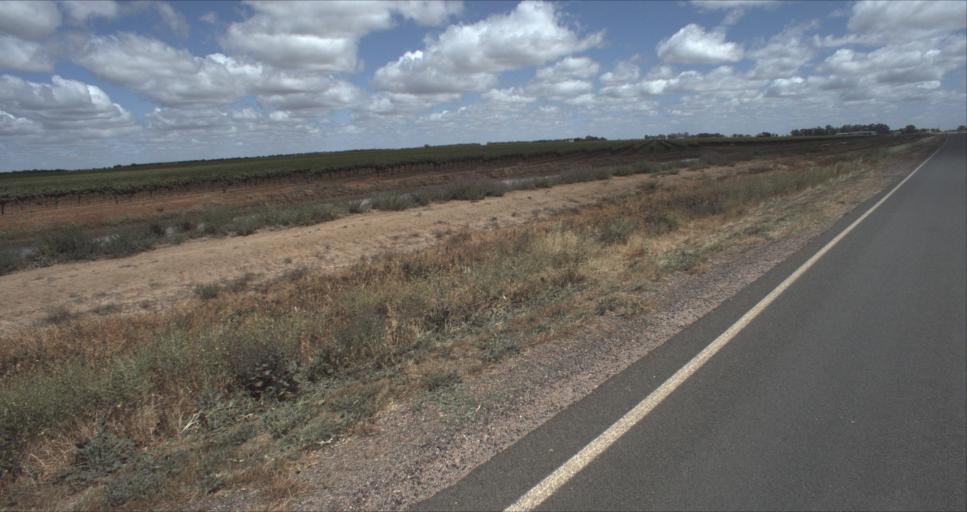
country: AU
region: New South Wales
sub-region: Murrumbidgee Shire
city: Darlington Point
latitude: -34.4934
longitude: 146.1672
